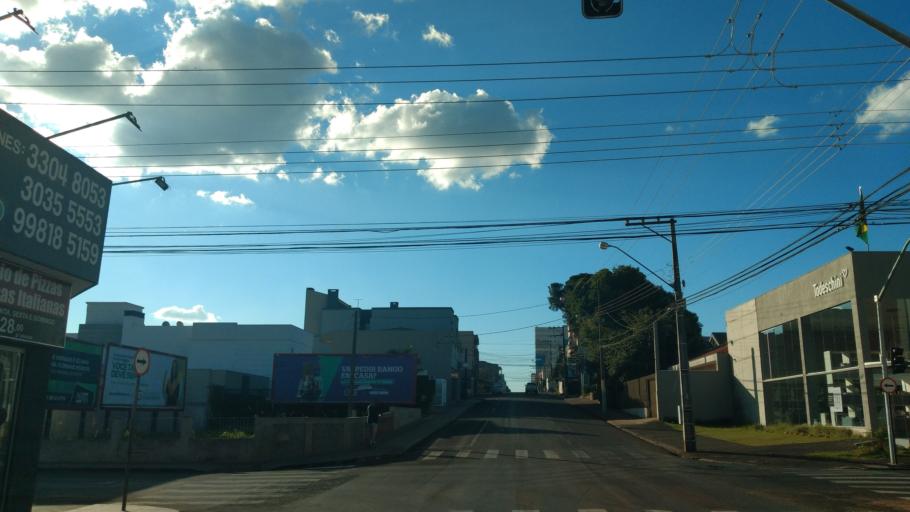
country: BR
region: Parana
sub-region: Guarapuava
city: Guarapuava
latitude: -25.3953
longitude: -51.4710
